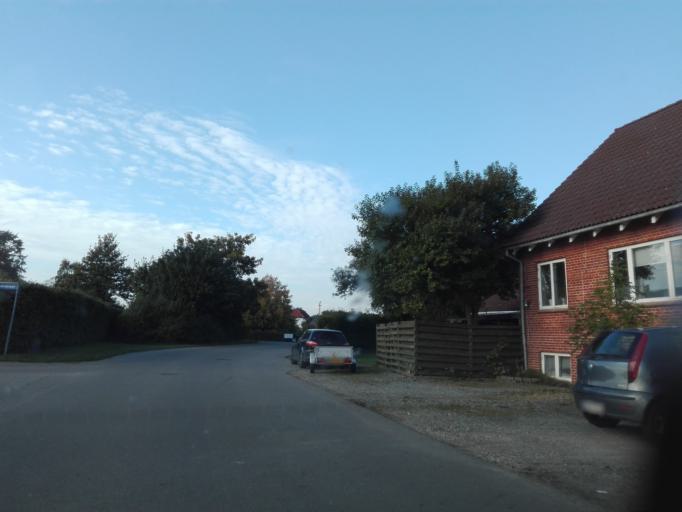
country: DK
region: Central Jutland
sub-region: Odder Kommune
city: Odder
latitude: 55.9563
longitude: 10.1893
